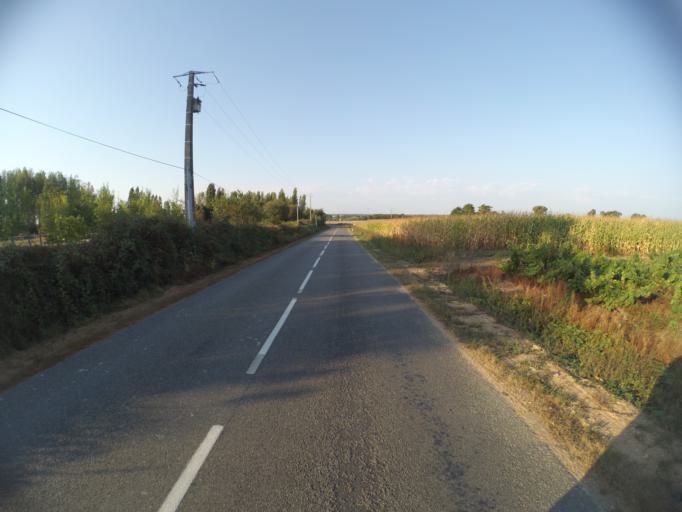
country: FR
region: Pays de la Loire
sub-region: Departement de la Loire-Atlantique
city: La Planche
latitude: 47.0309
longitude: -1.4204
